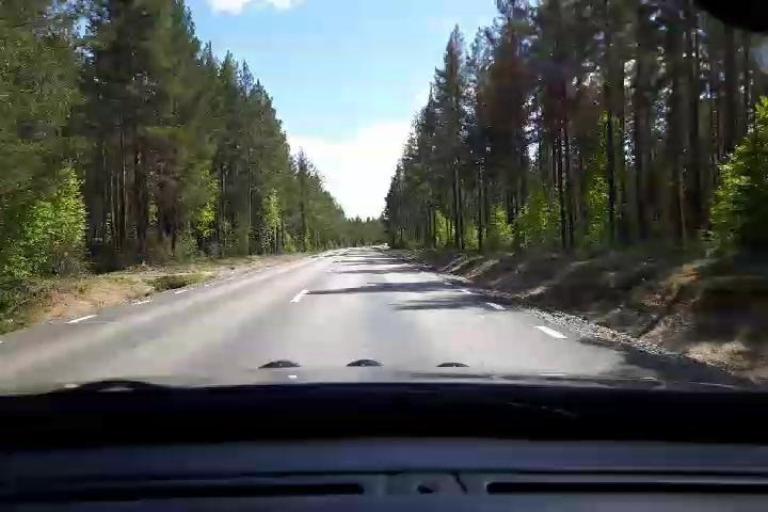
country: SE
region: Gaevleborg
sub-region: Ljusdals Kommun
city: Farila
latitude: 61.8533
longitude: 15.7490
